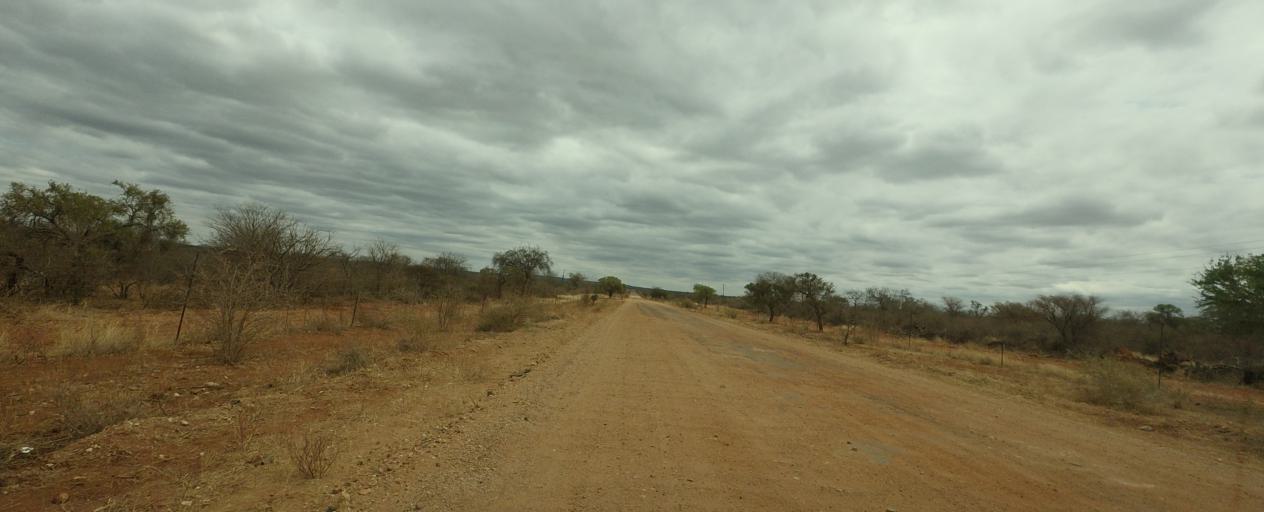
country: BW
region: Central
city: Mathathane
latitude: -22.7399
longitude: 28.4816
